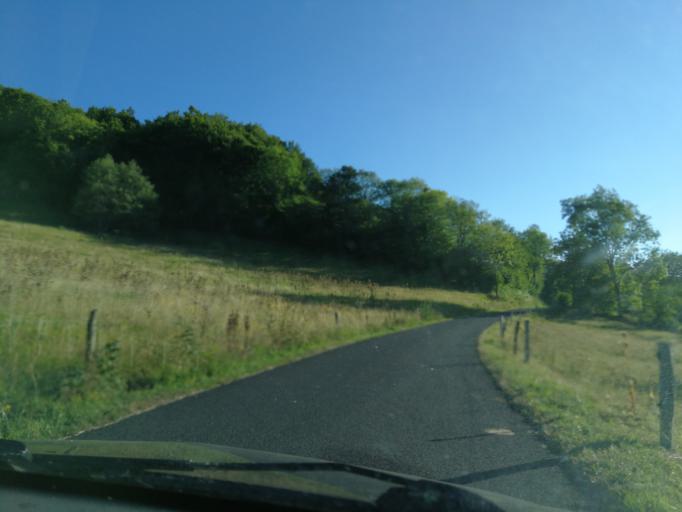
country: FR
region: Auvergne
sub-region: Departement du Cantal
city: Vic-sur-Cere
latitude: 45.0872
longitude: 2.5721
